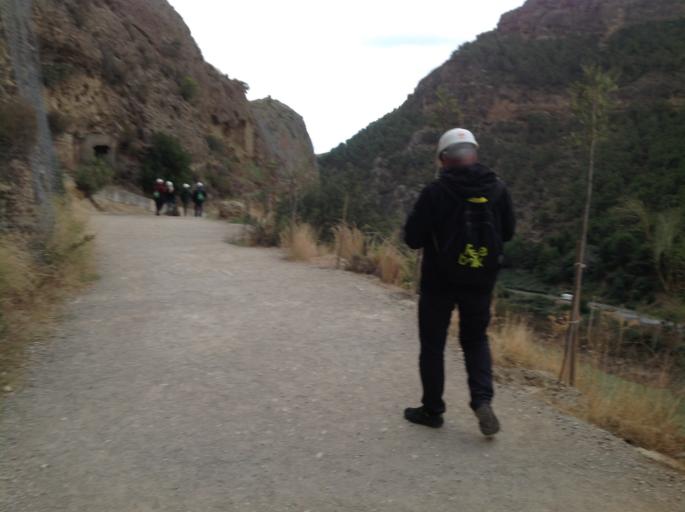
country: ES
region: Andalusia
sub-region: Provincia de Malaga
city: Carratraca
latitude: 36.9149
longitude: -4.7696
